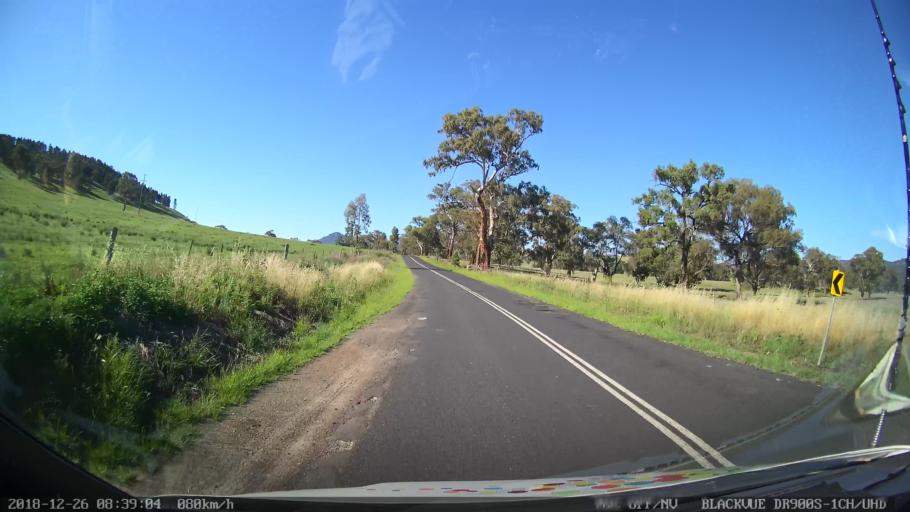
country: AU
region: New South Wales
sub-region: Upper Hunter Shire
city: Merriwa
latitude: -32.4490
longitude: 150.0769
